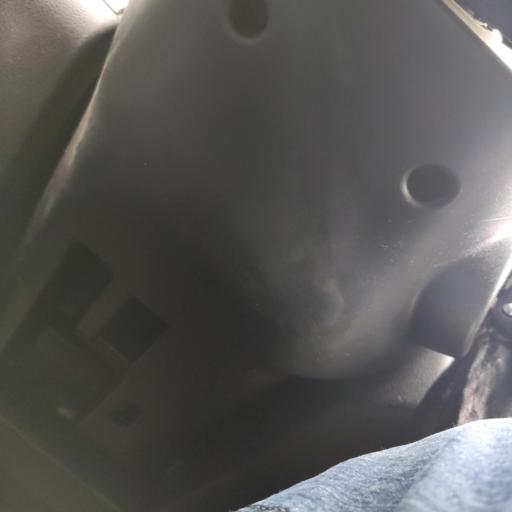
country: RU
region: Samara
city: Smyshlyayevka
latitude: 53.2090
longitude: 50.3243
